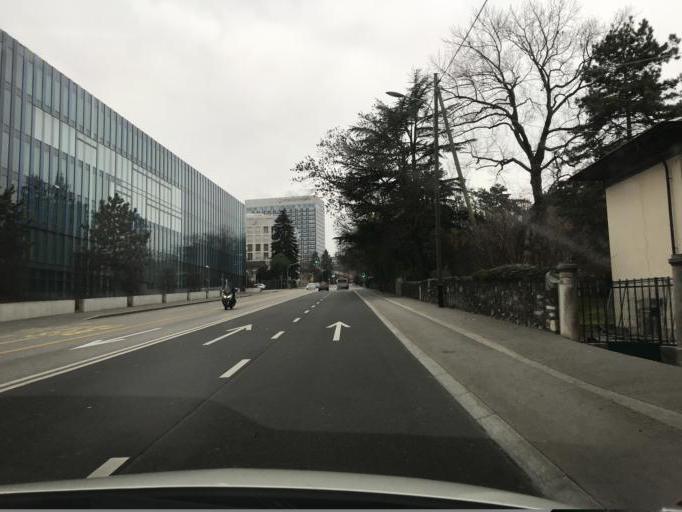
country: CH
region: Geneva
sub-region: Geneva
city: Le Grand-Saconnex
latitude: 46.2228
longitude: 6.1371
